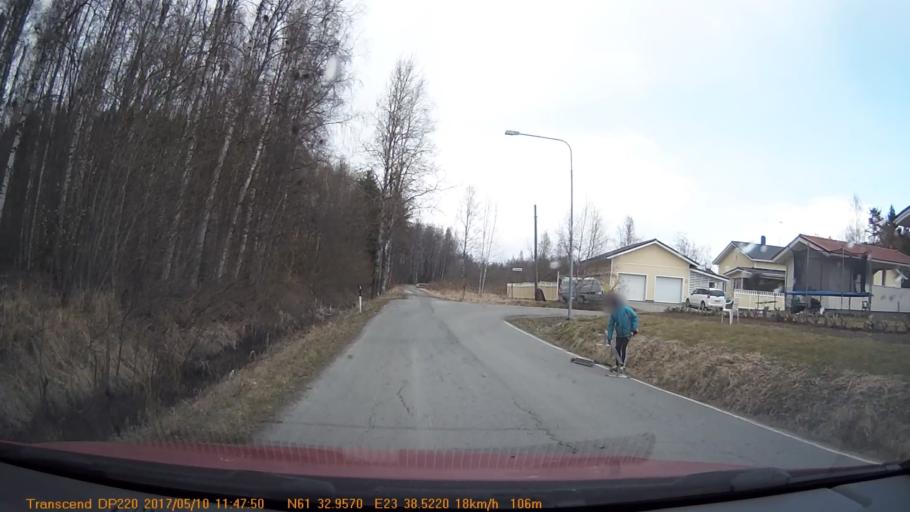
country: FI
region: Pirkanmaa
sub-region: Tampere
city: Yloejaervi
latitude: 61.5491
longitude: 23.6413
